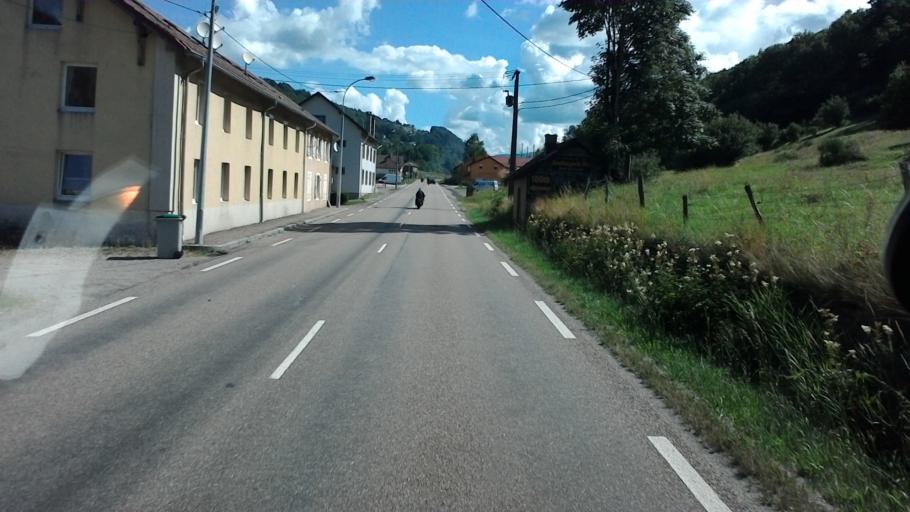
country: FR
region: Lorraine
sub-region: Departement des Vosges
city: Cornimont
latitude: 47.9866
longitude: 6.8395
